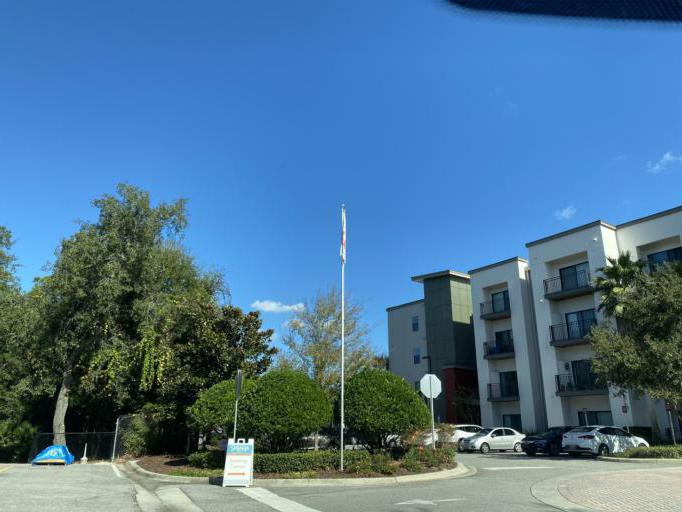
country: US
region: Florida
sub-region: Seminole County
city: Heathrow
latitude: 28.7883
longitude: -81.3450
